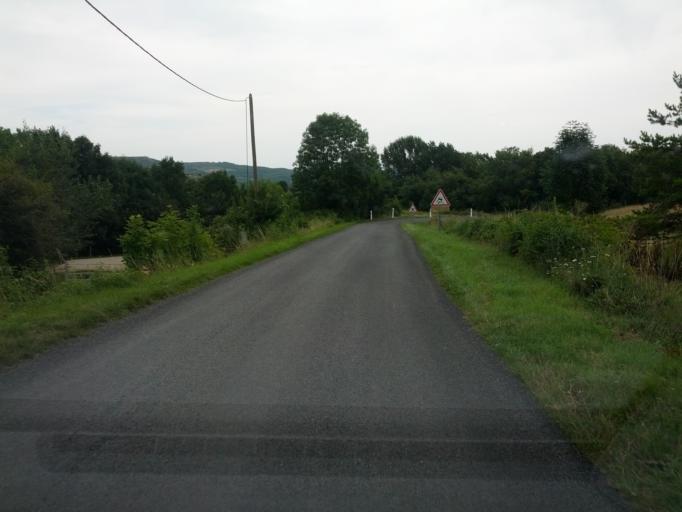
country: FR
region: Languedoc-Roussillon
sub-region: Departement de l'Aude
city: Quillan
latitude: 42.8862
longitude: 2.1437
